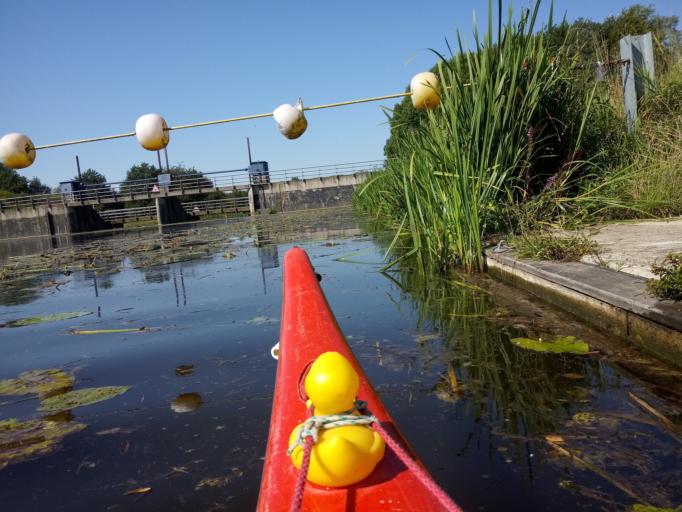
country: NL
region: Gelderland
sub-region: Berkelland
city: Eibergen
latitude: 52.1036
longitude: 6.6677
